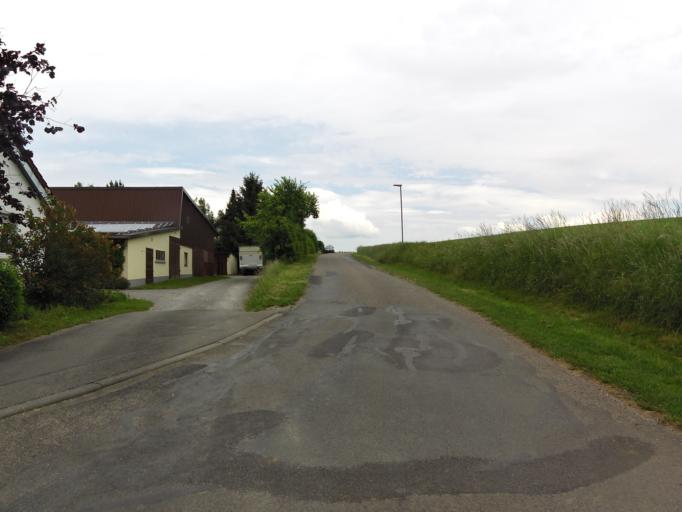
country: DE
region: Bavaria
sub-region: Regierungsbezirk Unterfranken
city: Waldbrunn
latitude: 49.7074
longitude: 9.7905
